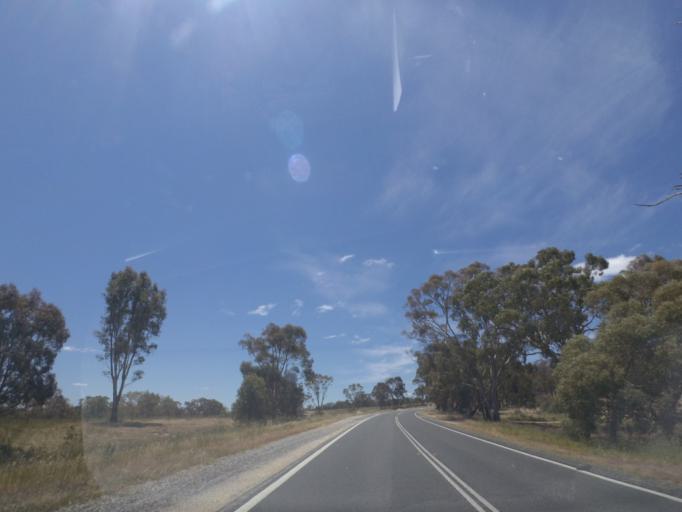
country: AU
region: Victoria
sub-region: Mount Alexander
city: Castlemaine
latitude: -37.1690
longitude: 144.1465
